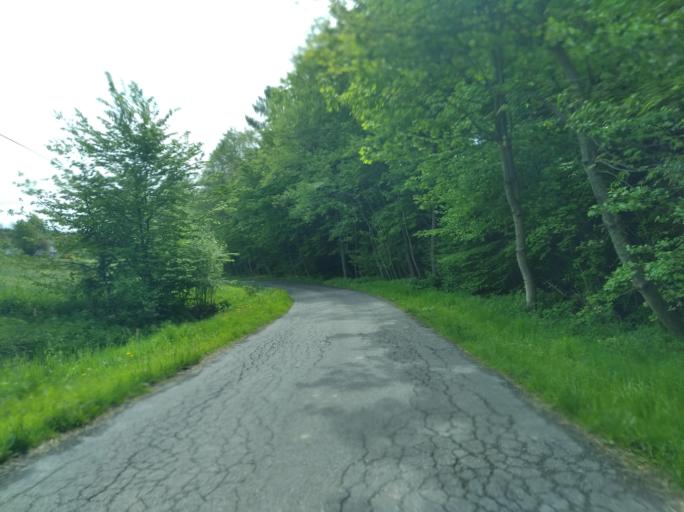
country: PL
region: Subcarpathian Voivodeship
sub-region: Powiat strzyzowski
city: Strzyzow
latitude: 49.9300
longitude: 21.7360
